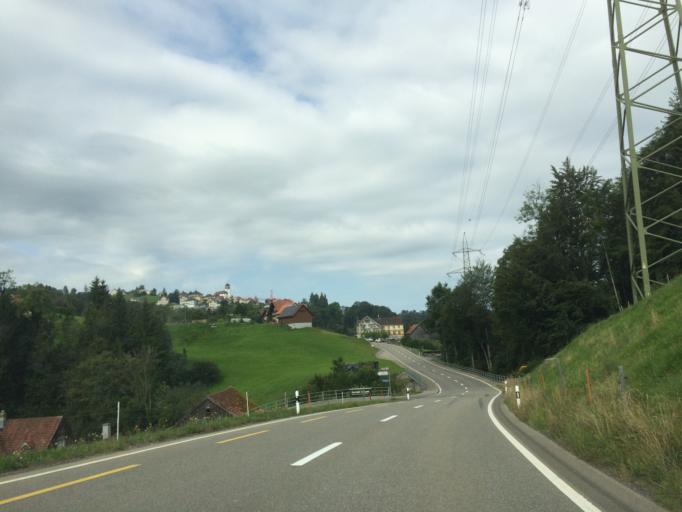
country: CH
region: Appenzell Ausserrhoden
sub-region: Bezirk Mittelland
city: Trogen
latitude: 47.4082
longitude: 9.4802
